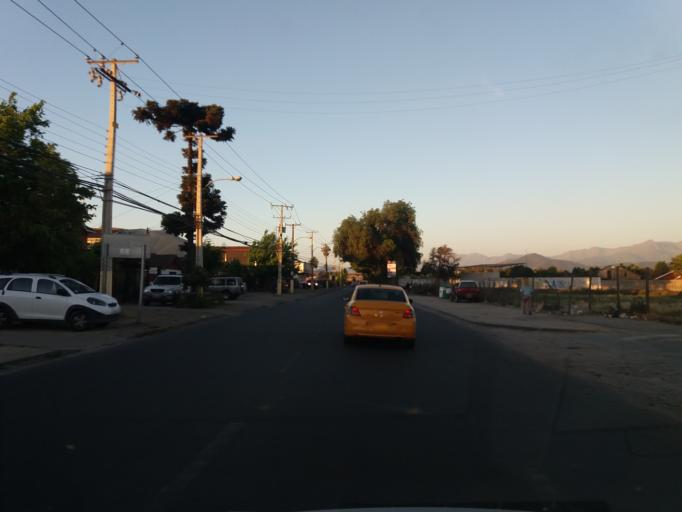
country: CL
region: Valparaiso
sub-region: Provincia de Quillota
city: Quillota
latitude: -32.8957
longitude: -71.2644
